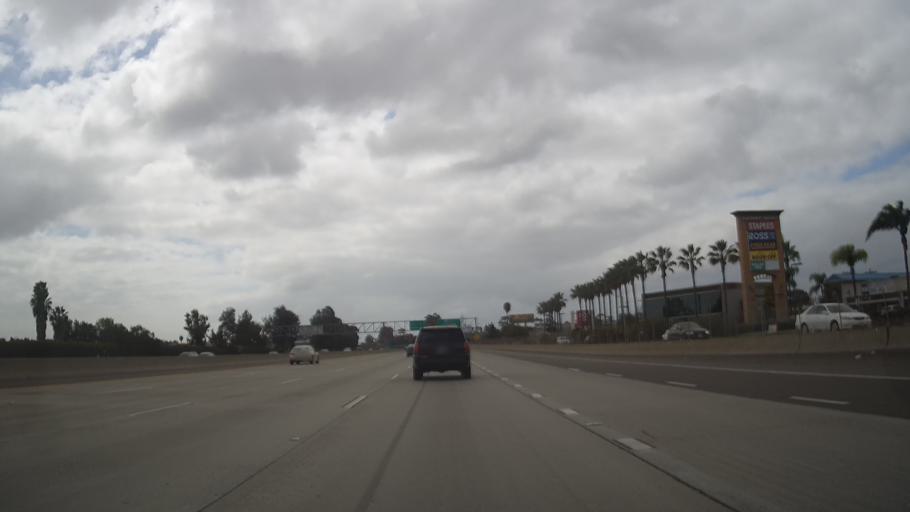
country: US
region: California
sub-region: San Diego County
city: San Diego
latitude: 32.8180
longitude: -117.1498
